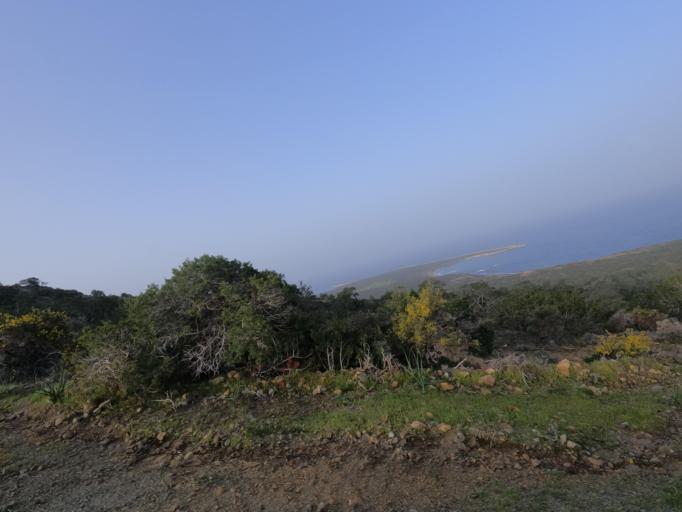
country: CY
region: Pafos
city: Pegeia
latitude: 34.9670
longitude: 32.3251
